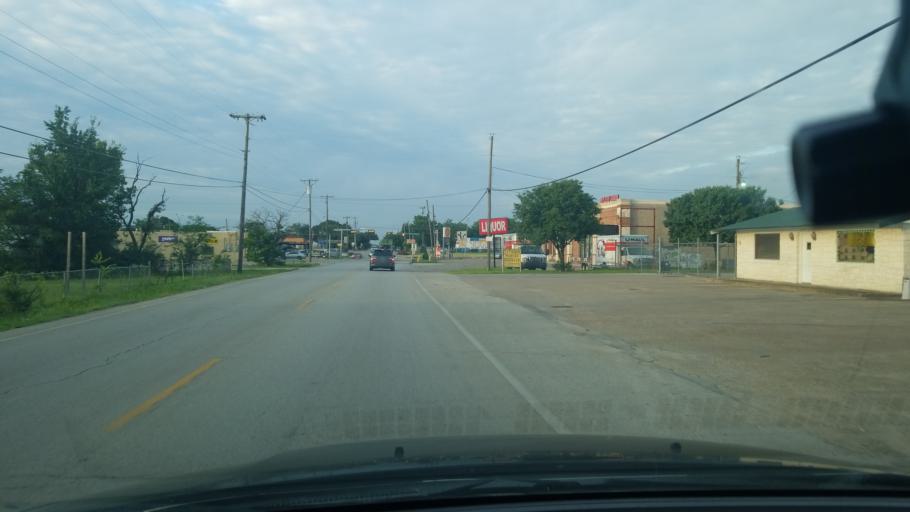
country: US
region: Texas
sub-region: Dallas County
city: Balch Springs
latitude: 32.7355
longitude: -96.6313
